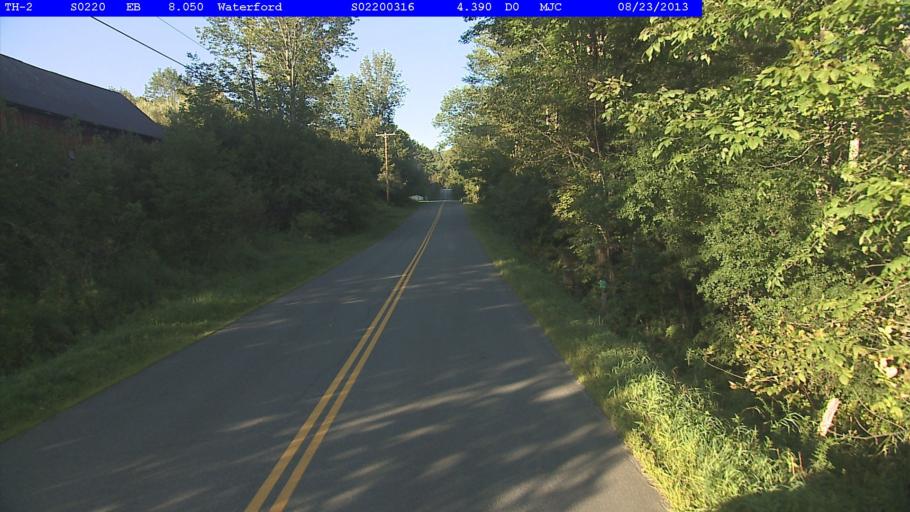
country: US
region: Vermont
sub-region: Caledonia County
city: Saint Johnsbury
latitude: 44.3497
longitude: -71.9201
